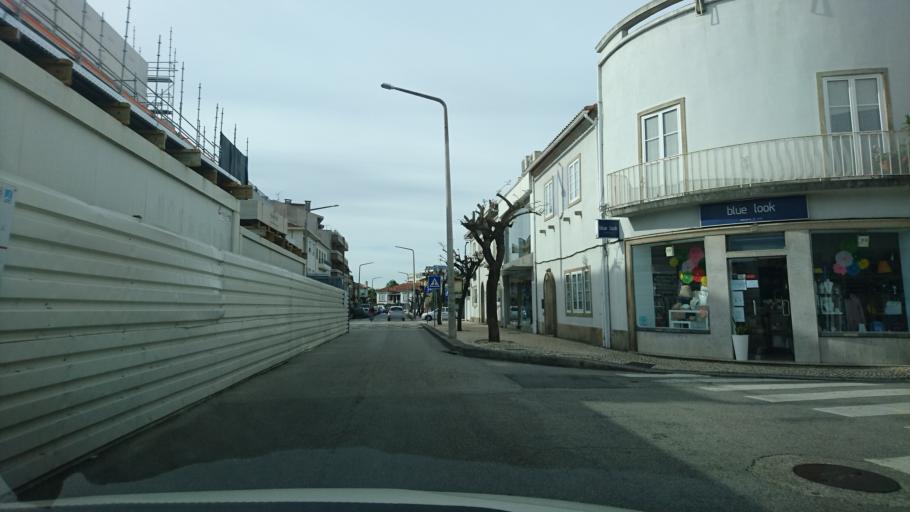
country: PT
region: Aveiro
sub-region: Oliveira de Azemeis
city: Oliveira de Azemeis
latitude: 40.8369
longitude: -8.4774
